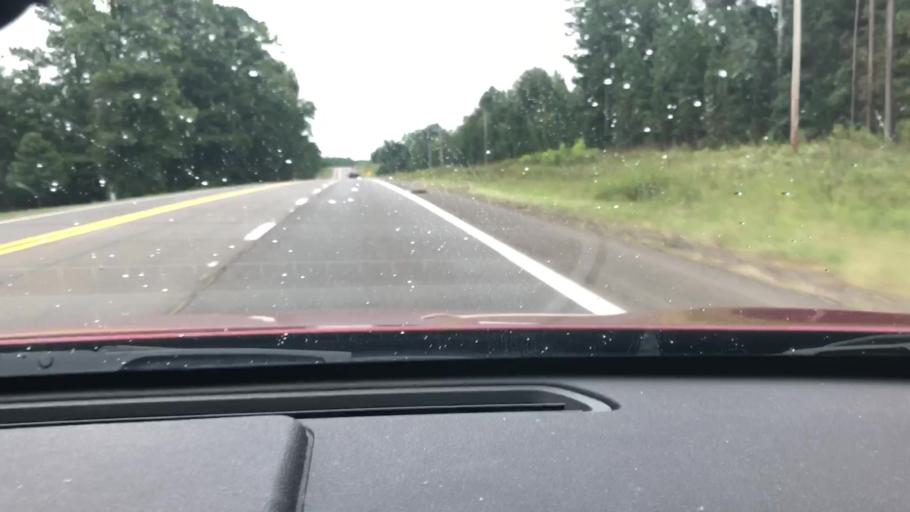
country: US
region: Arkansas
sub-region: Columbia County
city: Waldo
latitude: 33.3510
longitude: -93.3765
